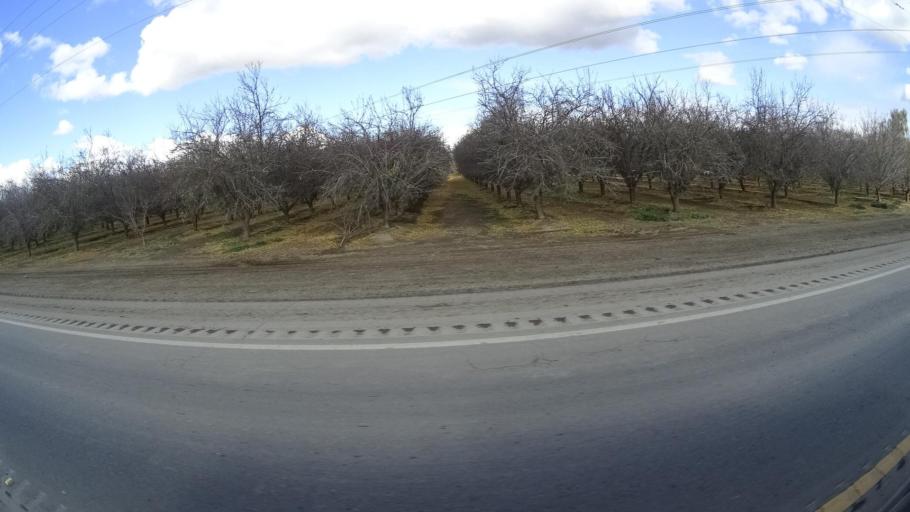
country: US
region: California
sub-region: Kern County
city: Greenfield
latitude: 35.2088
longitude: -119.0798
